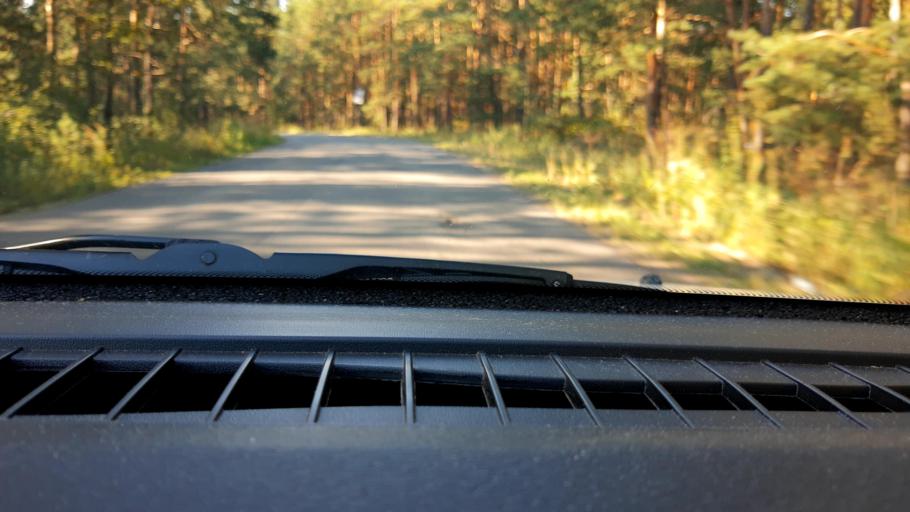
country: RU
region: Nizjnij Novgorod
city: Babino
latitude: 56.3274
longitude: 43.6330
